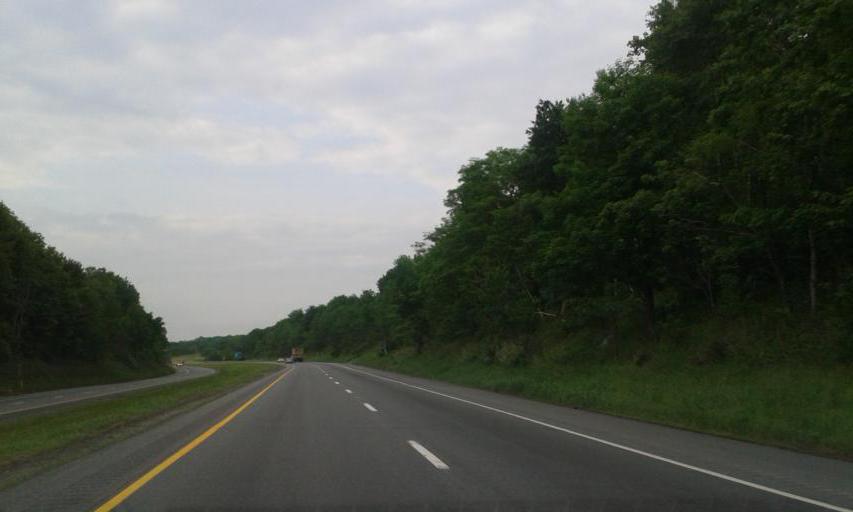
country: US
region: Pennsylvania
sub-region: Susquehanna County
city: Susquehanna
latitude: 41.8132
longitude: -75.6833
